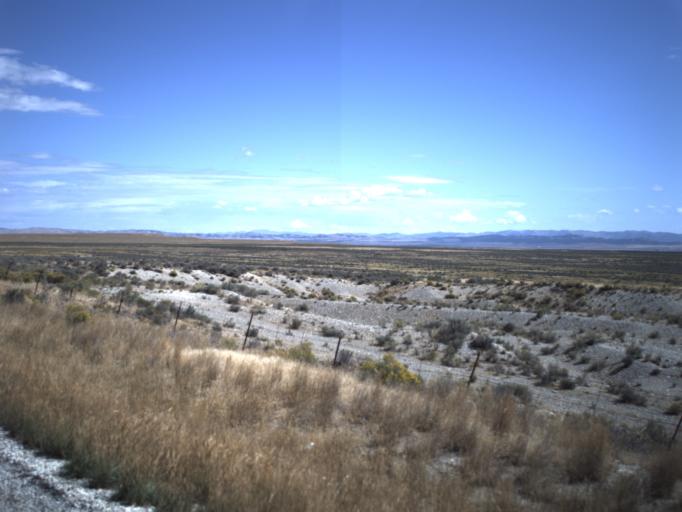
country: US
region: Idaho
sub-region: Oneida County
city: Malad City
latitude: 41.9403
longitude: -113.0843
